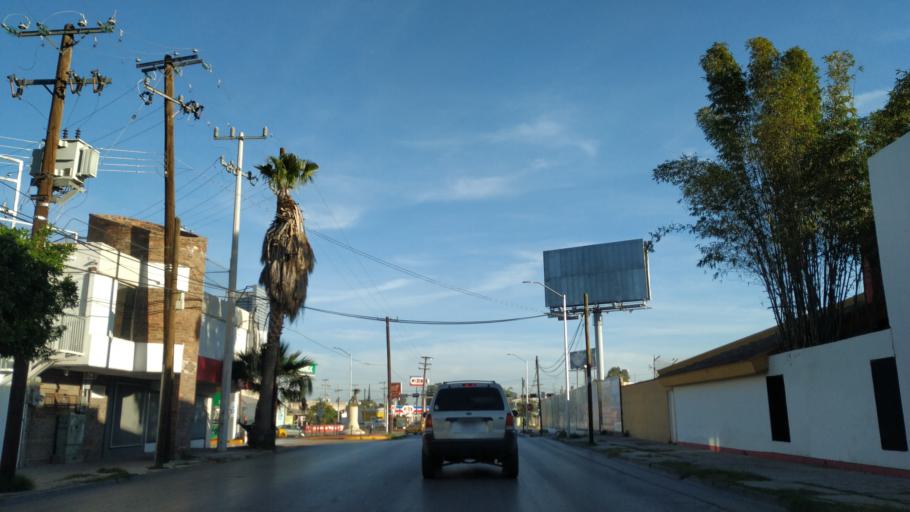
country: MX
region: Coahuila
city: Torreon
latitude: 25.5496
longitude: -103.4486
